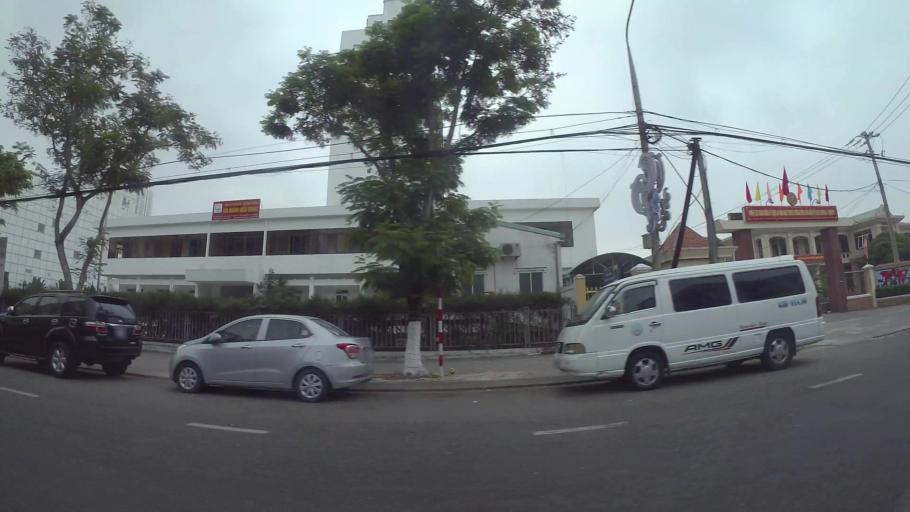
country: VN
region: Da Nang
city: Son Tra
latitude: 16.0553
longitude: 108.2430
